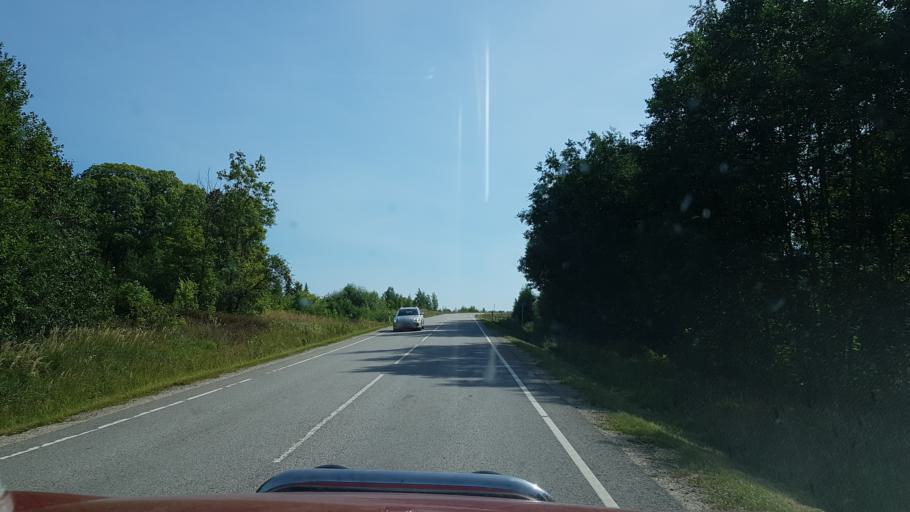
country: EE
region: Viljandimaa
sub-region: Vohma linn
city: Vohma
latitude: 58.5195
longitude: 25.6328
